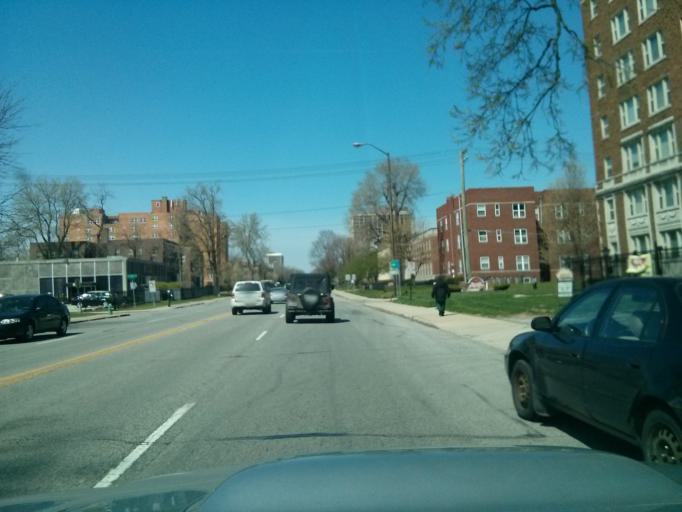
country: US
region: Indiana
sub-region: Marion County
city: Broad Ripple
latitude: 39.8206
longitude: -86.1567
